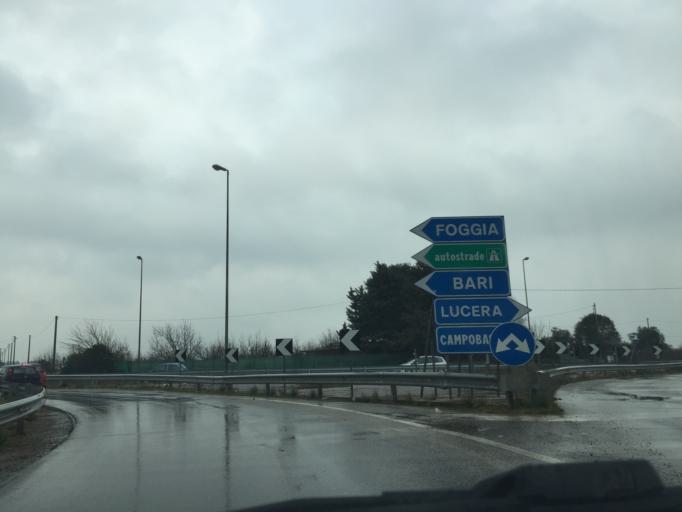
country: IT
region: Apulia
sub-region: Provincia di Foggia
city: Foggia
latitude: 41.4719
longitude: 15.5068
